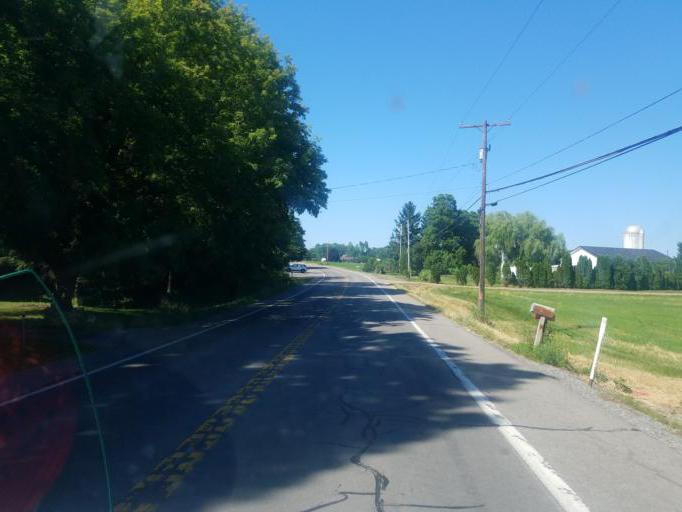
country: US
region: New York
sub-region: Wayne County
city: Newark
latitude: 43.0080
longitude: -77.0936
